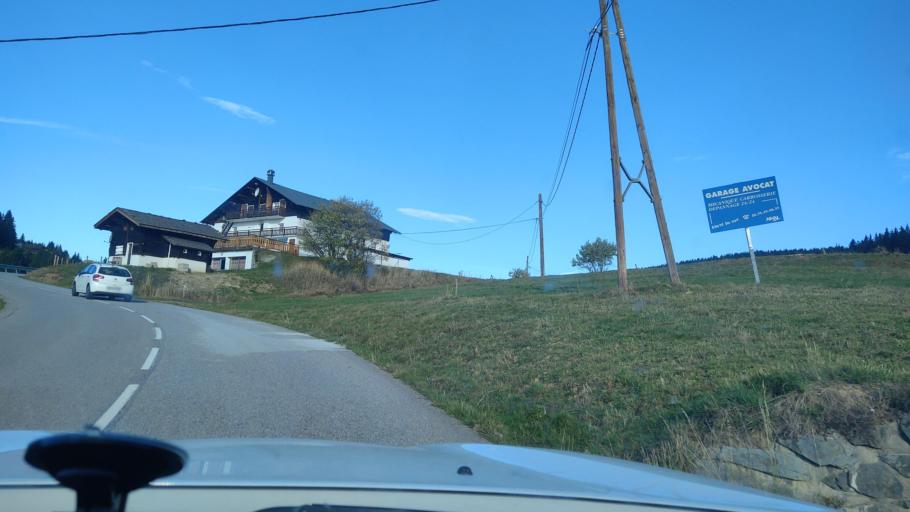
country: FR
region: Rhone-Alpes
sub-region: Departement de la Savoie
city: Beaufort
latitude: 45.7472
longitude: 6.5488
